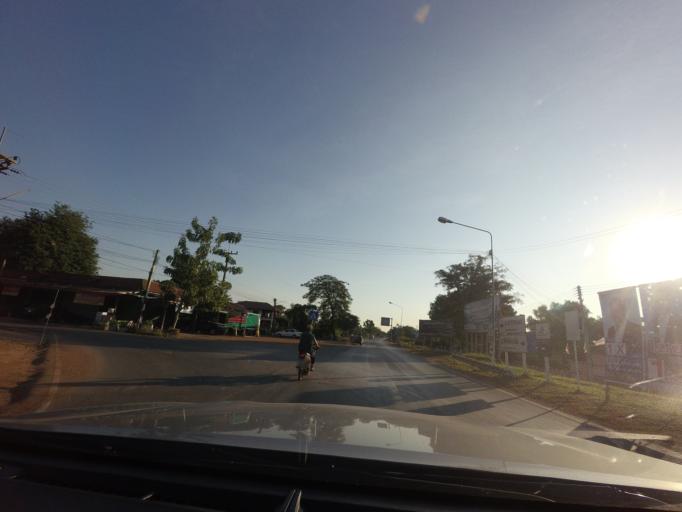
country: TH
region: Sukhothai
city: Sawankhalok
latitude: 17.3946
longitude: 99.7957
